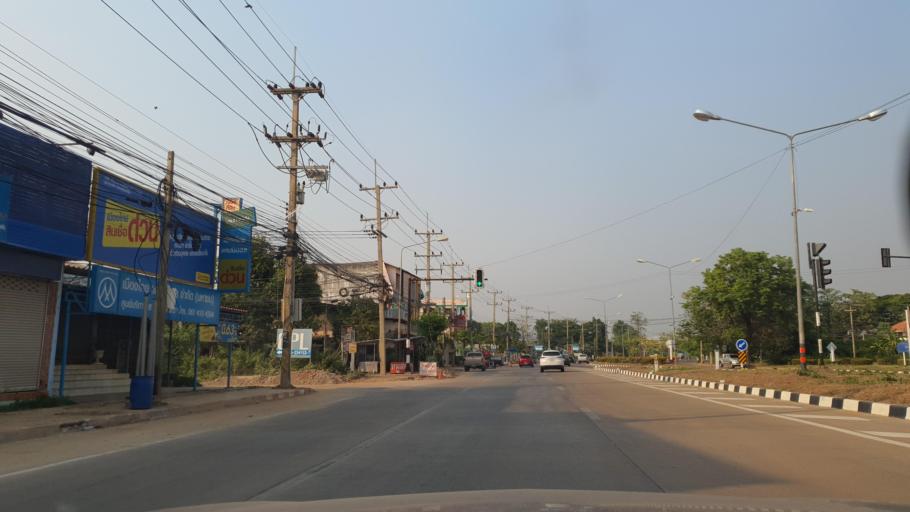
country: TH
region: Phitsanulok
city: Phitsanulok
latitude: 16.8011
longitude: 100.2148
